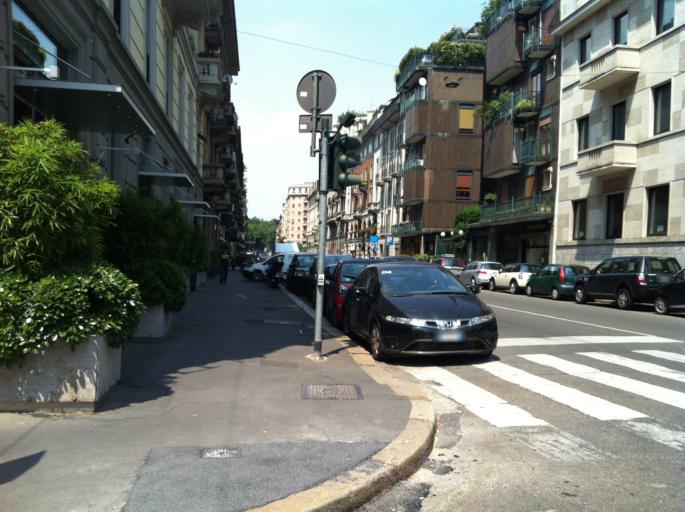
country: IT
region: Lombardy
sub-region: Citta metropolitana di Milano
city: Milano
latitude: 45.4724
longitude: 9.2112
